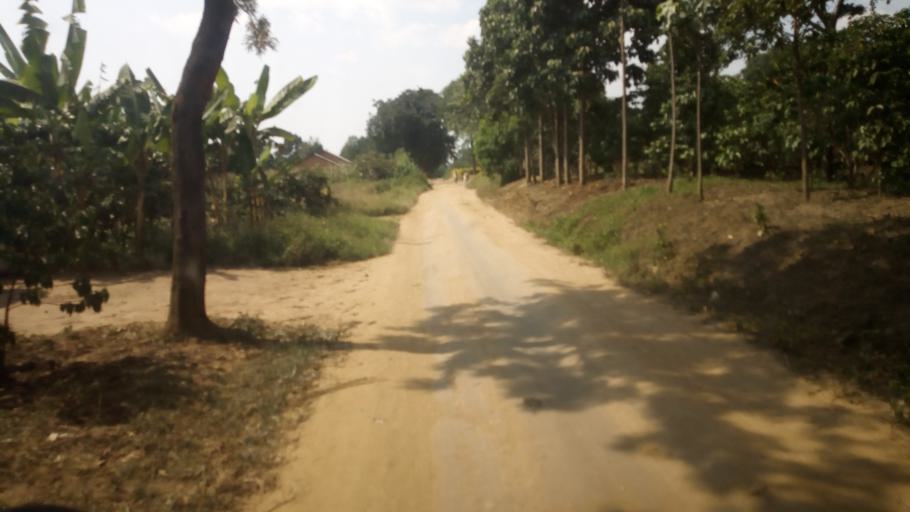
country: UG
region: Western Region
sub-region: Kanungu District
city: Ntungamo
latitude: -0.7883
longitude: 29.6880
